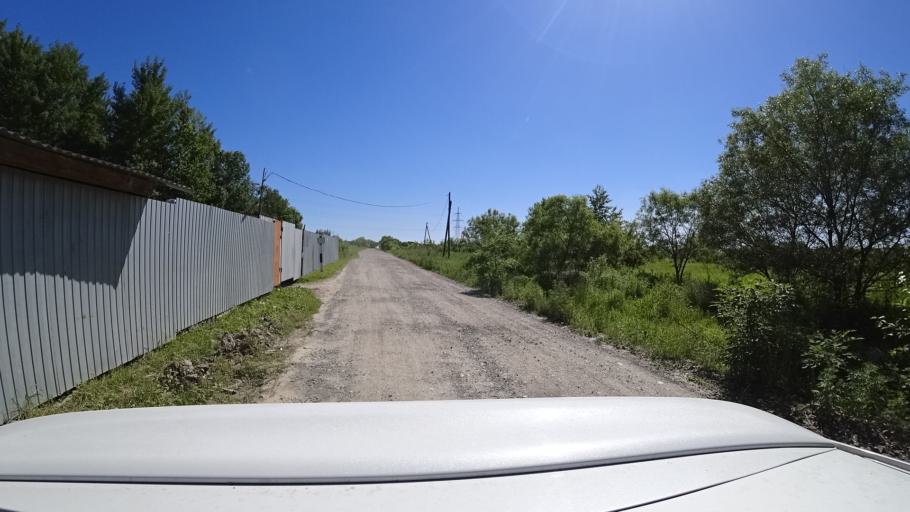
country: RU
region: Khabarovsk Krai
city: Topolevo
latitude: 48.5651
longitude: 135.1975
